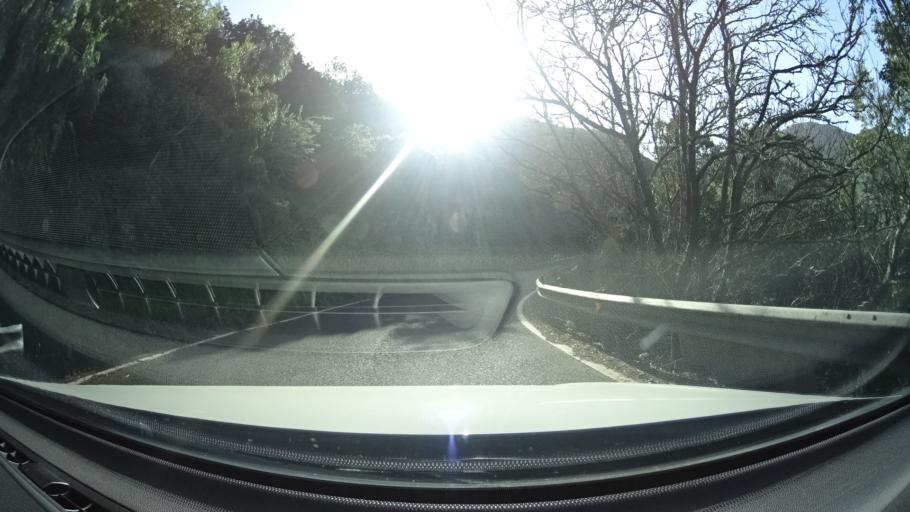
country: ES
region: Canary Islands
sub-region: Provincia de Las Palmas
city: Valleseco
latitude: 28.0289
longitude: -15.5561
